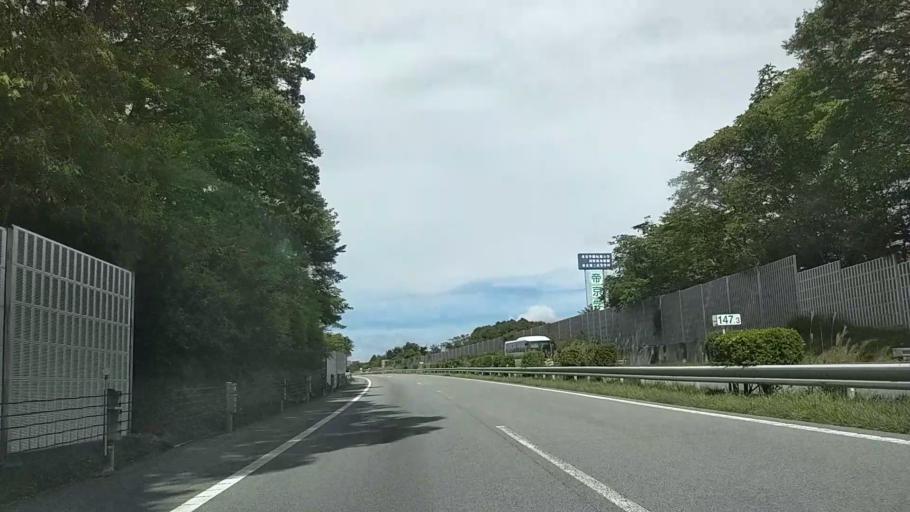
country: JP
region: Yamanashi
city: Nirasaki
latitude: 35.8669
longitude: 138.3228
